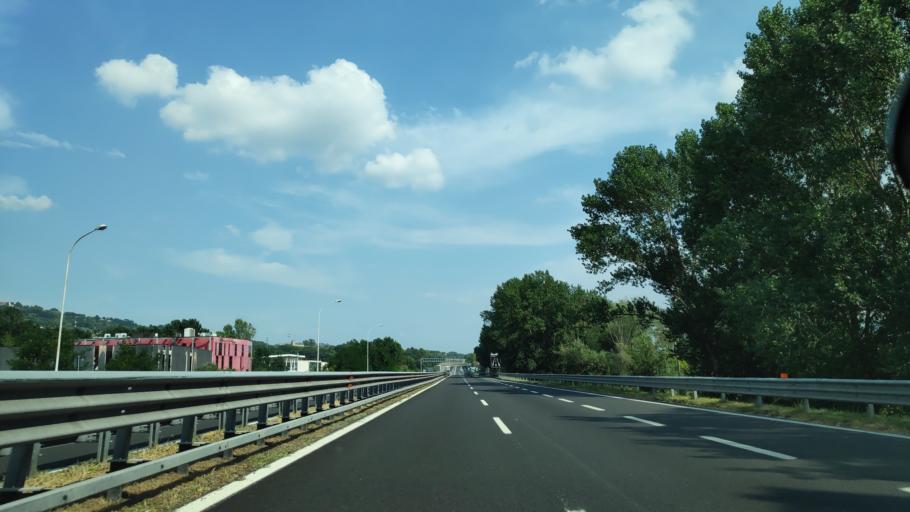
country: IT
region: Umbria
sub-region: Provincia di Terni
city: Attigliano
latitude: 42.5080
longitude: 12.2960
